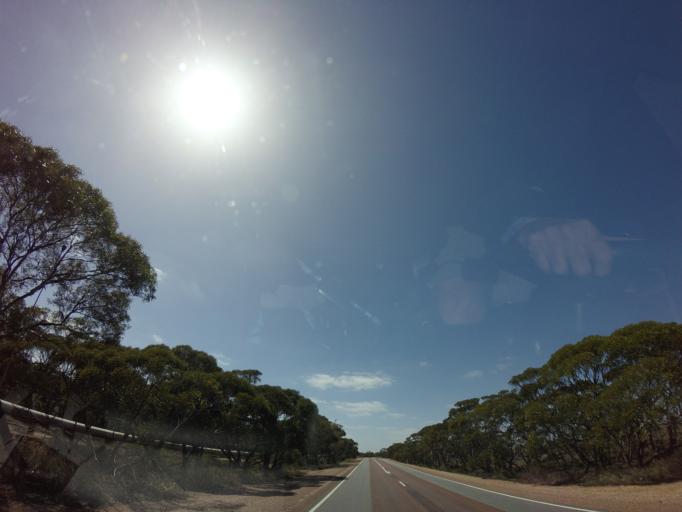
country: AU
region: South Australia
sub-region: Kimba
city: Caralue
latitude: -33.0779
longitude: 135.4915
